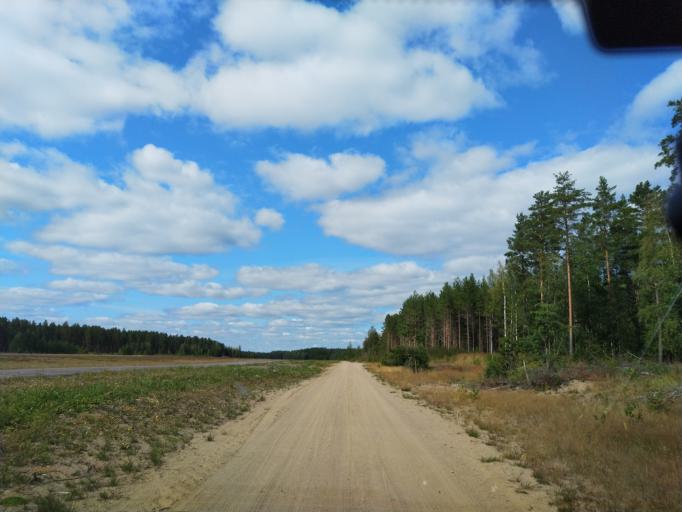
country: FI
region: Uusimaa
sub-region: Helsinki
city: Kaerkoelae
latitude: 60.7474
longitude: 24.1093
